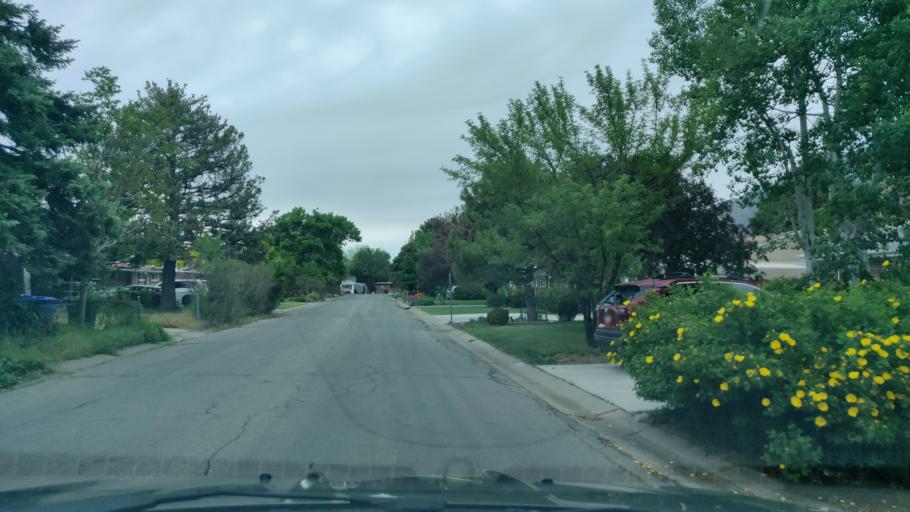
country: US
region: Utah
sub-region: Salt Lake County
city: Little Cottonwood Creek Valley
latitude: 40.6108
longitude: -111.8231
